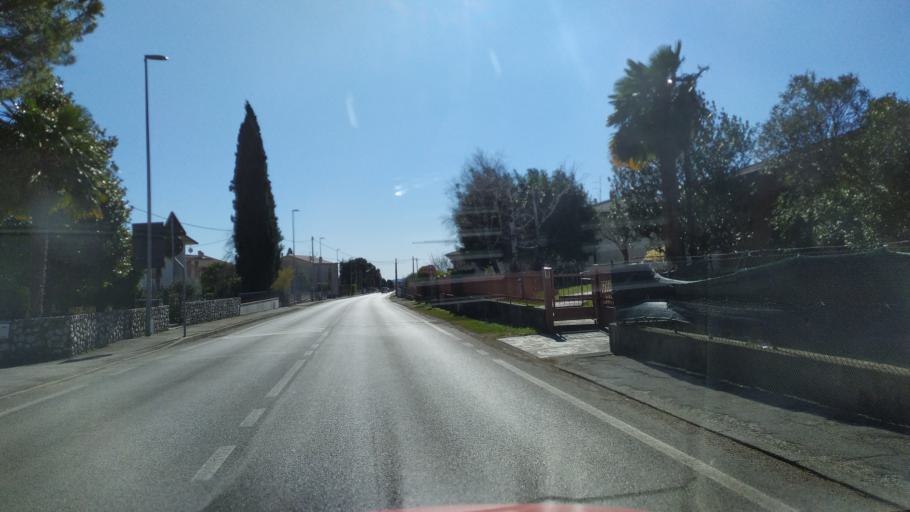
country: IT
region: Veneto
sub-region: Provincia di Vicenza
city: Chiuppano
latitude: 45.7602
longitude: 11.4583
